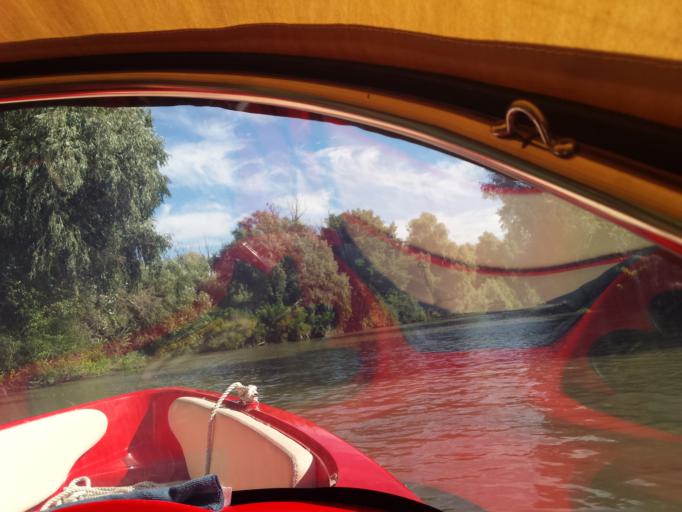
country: RO
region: Tulcea
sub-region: Comuna Pardina
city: Pardina
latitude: 45.2455
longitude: 29.0137
